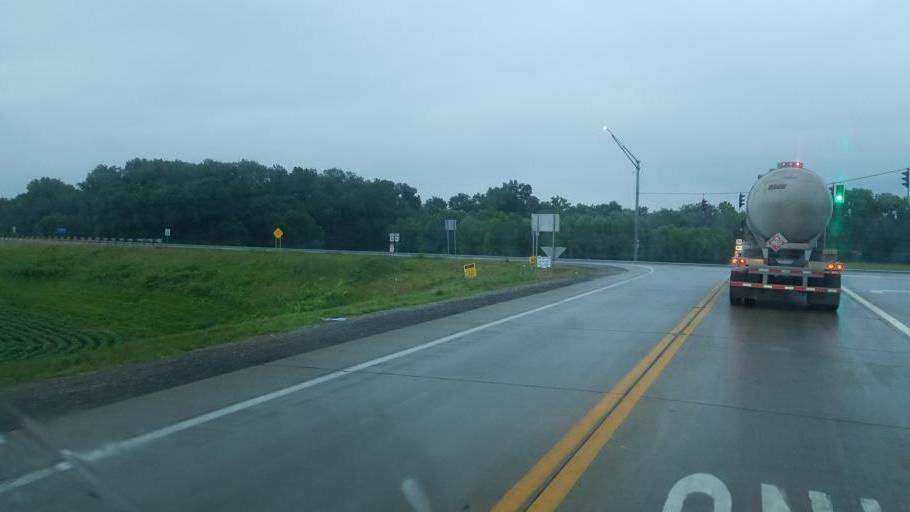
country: US
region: Ohio
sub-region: Coshocton County
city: Coshocton
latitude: 40.2833
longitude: -81.8738
